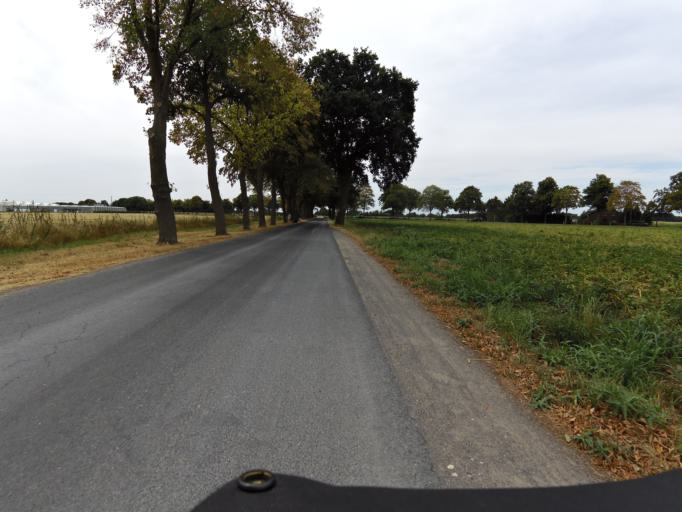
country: DE
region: North Rhine-Westphalia
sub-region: Regierungsbezirk Dusseldorf
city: Kevelaer
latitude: 51.5638
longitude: 6.2454
